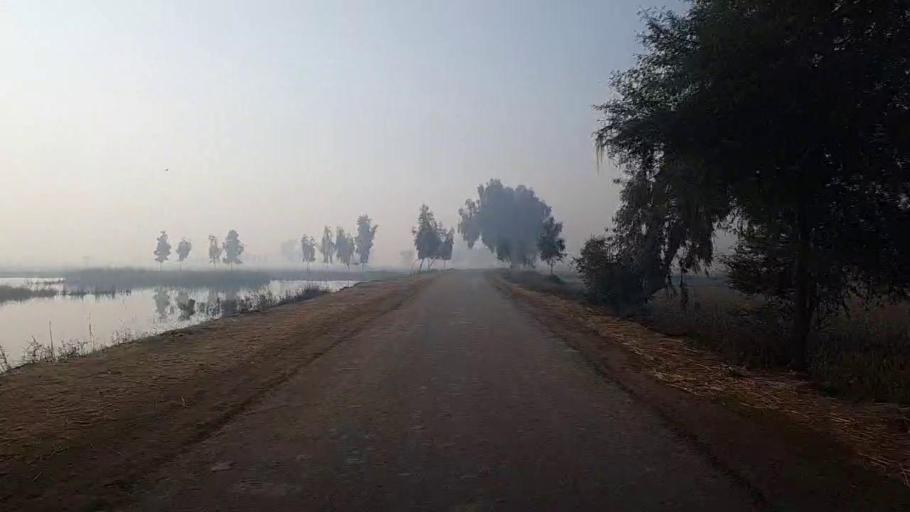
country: PK
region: Sindh
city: Mehar
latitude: 27.1462
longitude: 67.8229
